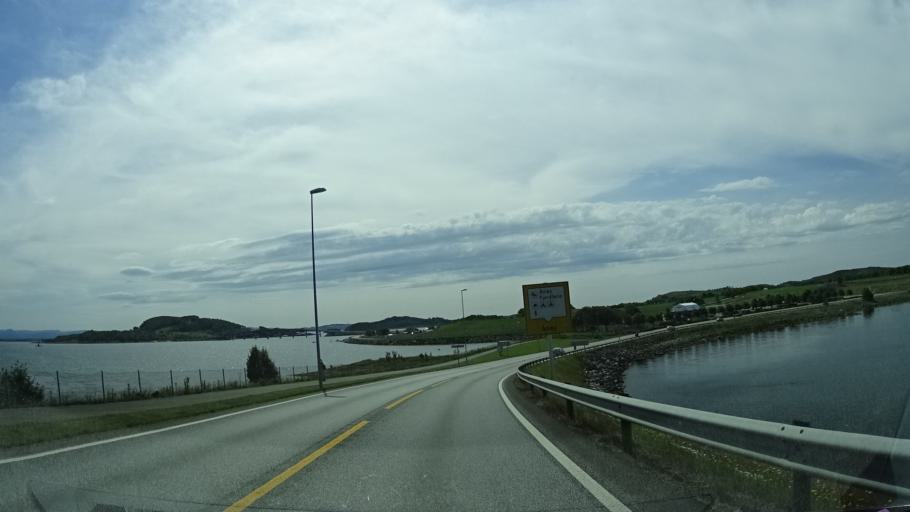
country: NO
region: Rogaland
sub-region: Rennesoy
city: Vikevag
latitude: 59.0585
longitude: 5.6773
